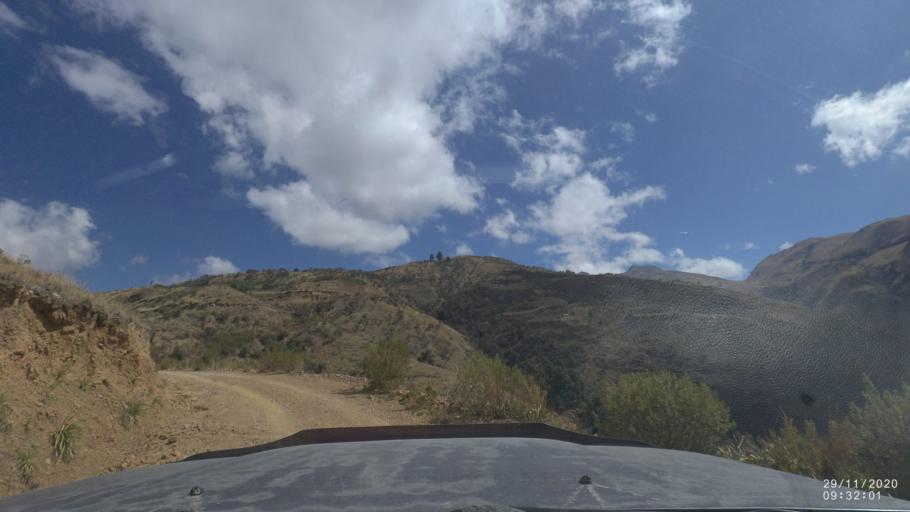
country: BO
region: Cochabamba
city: Cochabamba
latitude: -17.3149
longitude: -66.1875
